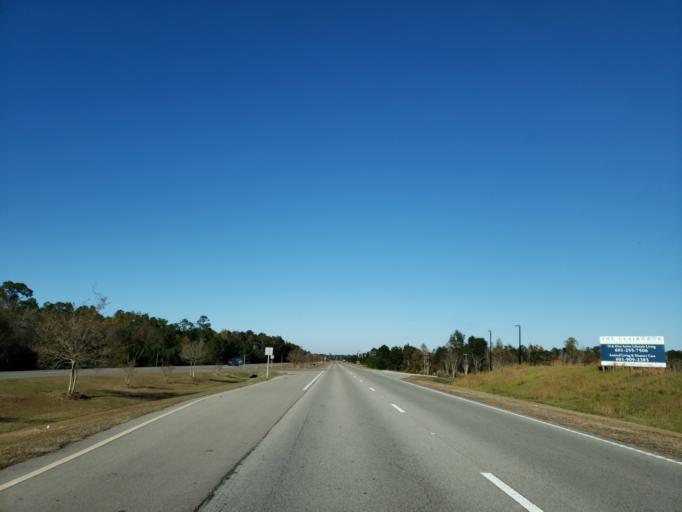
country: US
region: Mississippi
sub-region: Lamar County
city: West Hattiesburg
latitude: 31.2752
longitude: -89.3286
